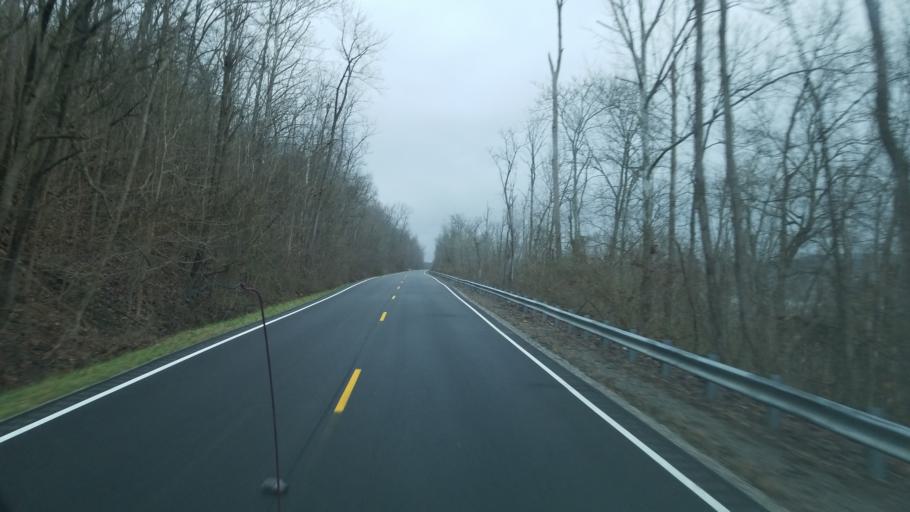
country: US
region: Kentucky
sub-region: Bracken County
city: Augusta
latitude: 38.7683
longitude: -83.9280
